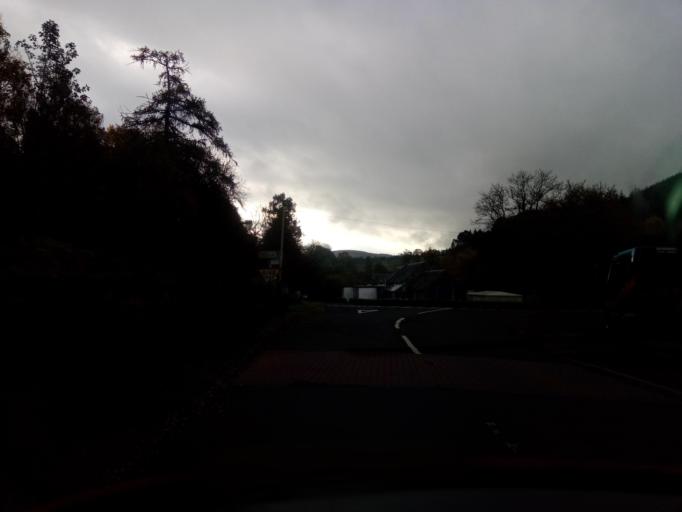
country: GB
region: Scotland
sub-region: The Scottish Borders
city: Selkirk
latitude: 55.6058
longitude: -2.8767
